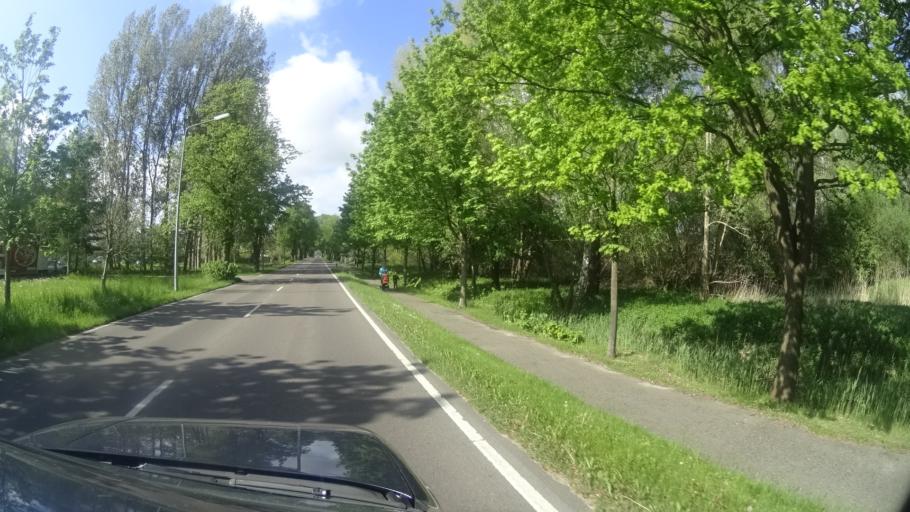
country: DE
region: Mecklenburg-Vorpommern
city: Dierkow-Neu
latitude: 54.0845
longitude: 12.1649
